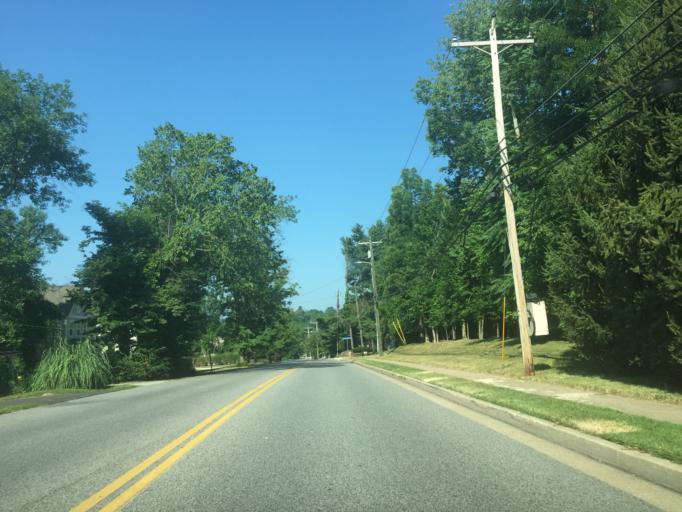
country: US
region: Maryland
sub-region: Baltimore County
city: Lutherville
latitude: 39.3739
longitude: -76.6451
